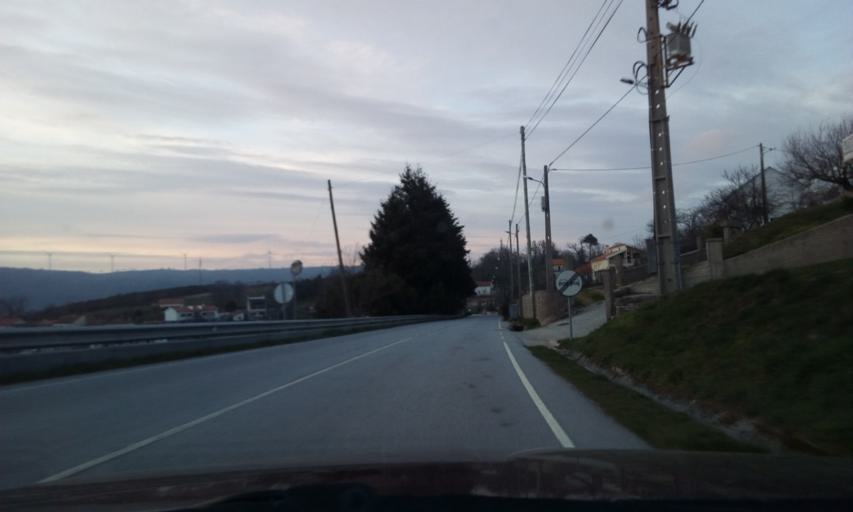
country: PT
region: Guarda
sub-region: Guarda
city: Guarda
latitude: 40.5423
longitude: -7.3173
